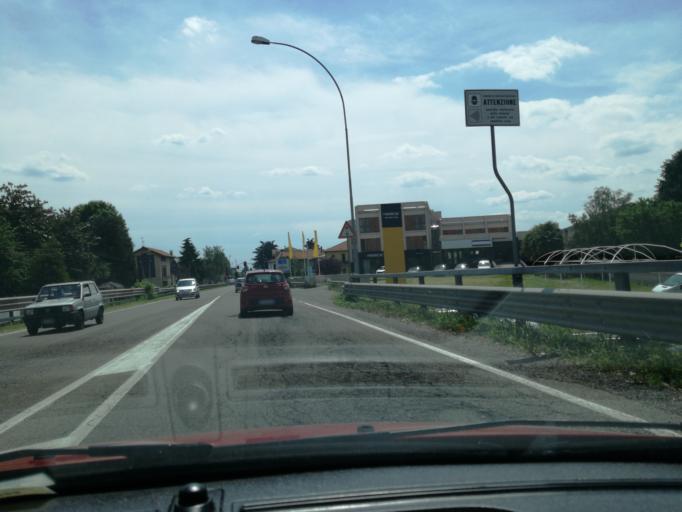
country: IT
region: Lombardy
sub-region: Provincia di Monza e Brianza
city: Bovisio-Masciago
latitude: 45.6163
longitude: 9.1366
